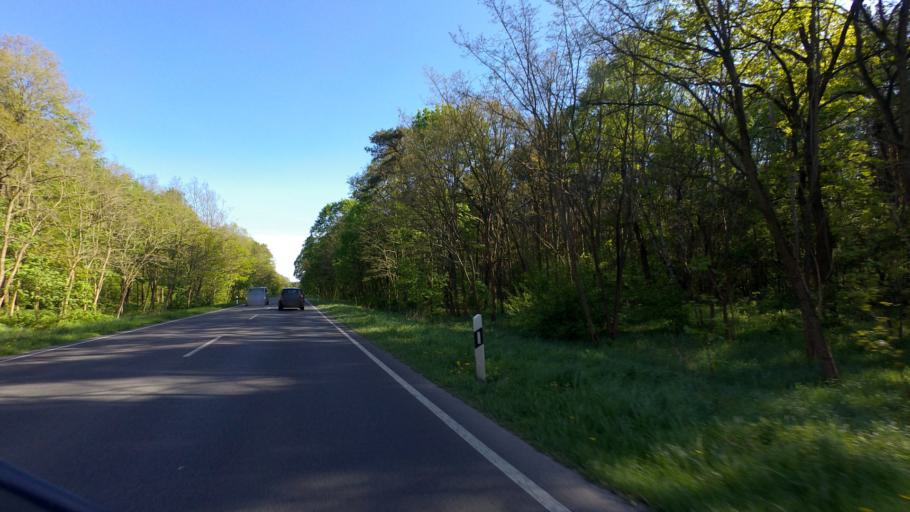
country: DE
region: Brandenburg
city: Oranienburg
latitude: 52.7198
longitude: 13.2530
